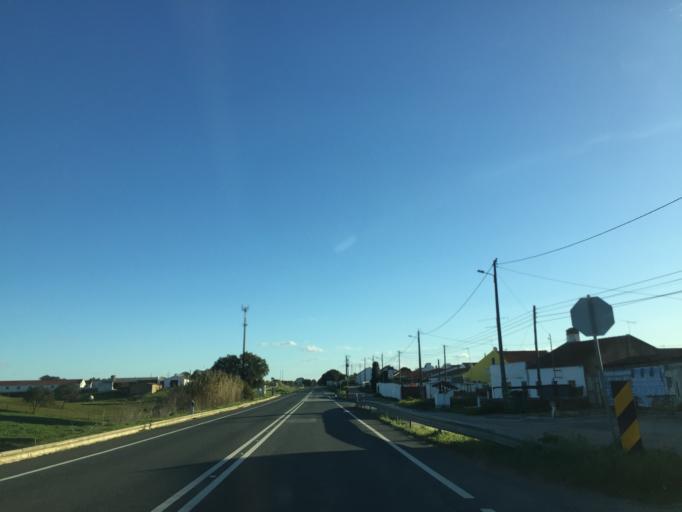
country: PT
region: Setubal
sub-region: Grandola
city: Grandola
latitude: 38.0506
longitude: -8.4022
